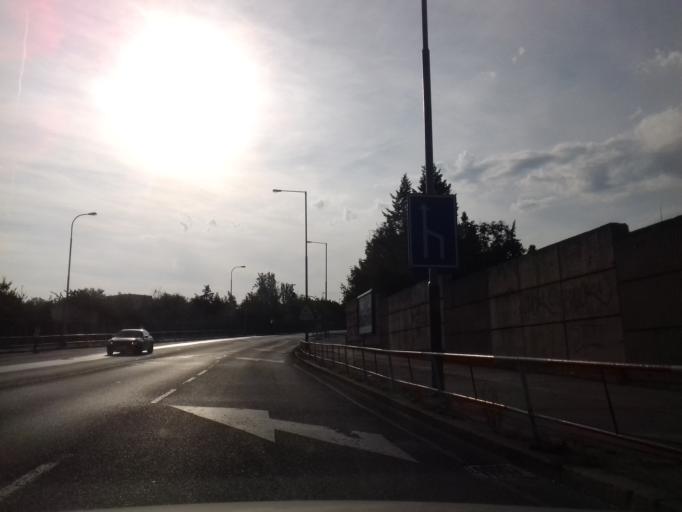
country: CZ
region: Praha
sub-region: Praha 4
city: Hodkovicky
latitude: 50.0281
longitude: 14.4567
